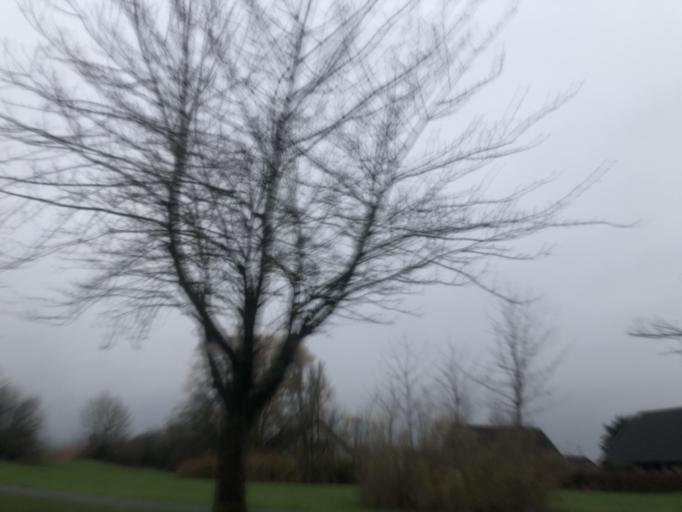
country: SE
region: Skane
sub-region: Trelleborgs Kommun
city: Trelleborg
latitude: 55.3884
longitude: 13.1659
